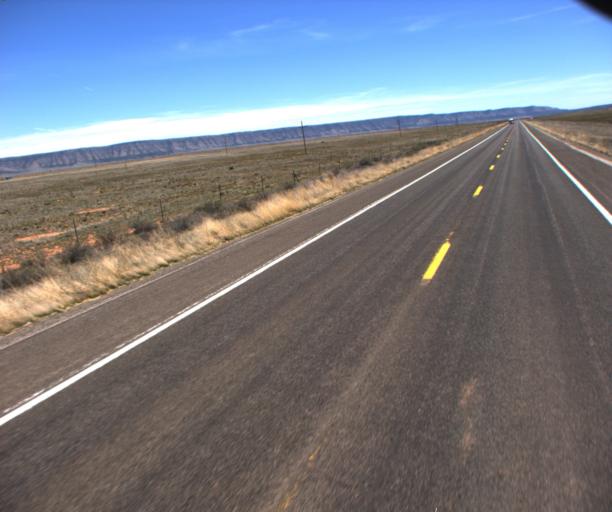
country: US
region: Arizona
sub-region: Mohave County
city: Peach Springs
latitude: 35.4712
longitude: -113.1265
